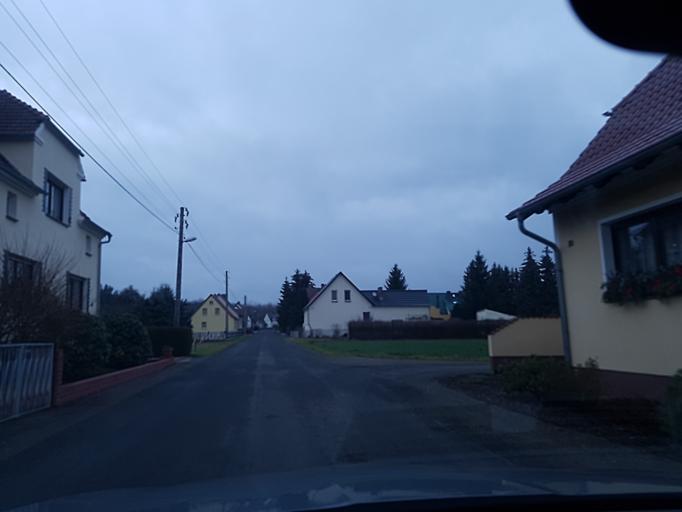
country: DE
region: Brandenburg
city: Schonborn
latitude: 51.5973
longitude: 13.4905
